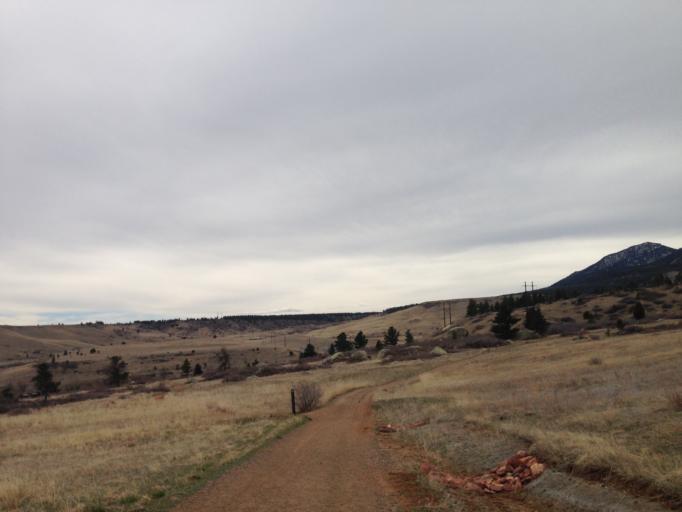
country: US
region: Colorado
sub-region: Boulder County
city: Boulder
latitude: 39.9447
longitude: -105.2633
